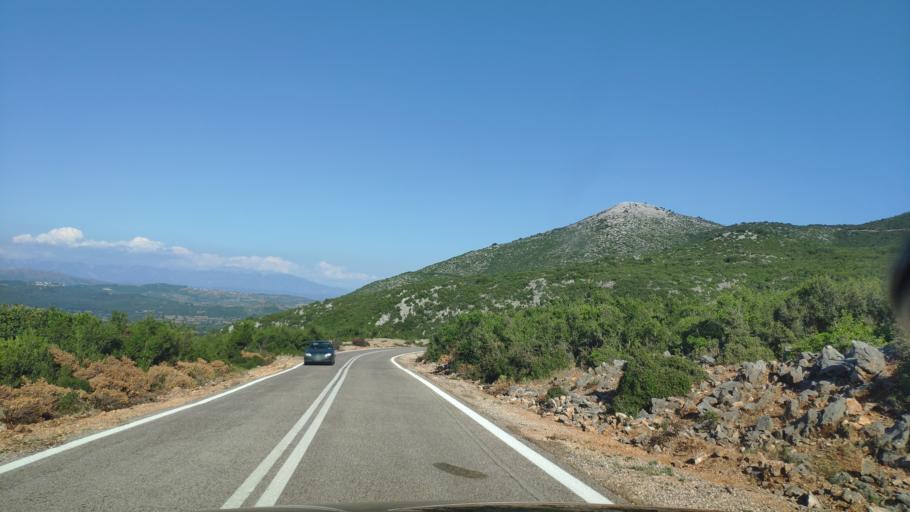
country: GR
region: West Greece
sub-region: Nomos Aitolias kai Akarnanias
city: Archontochorion
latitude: 38.6928
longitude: 21.0788
